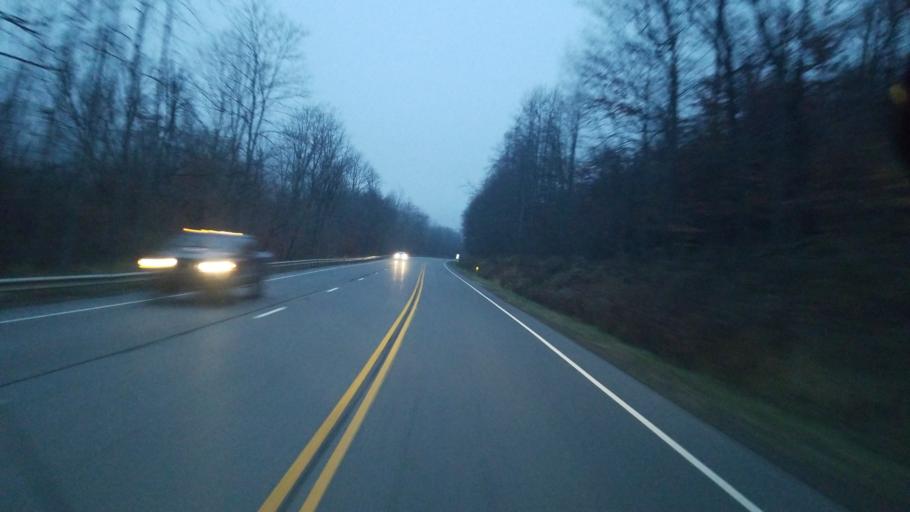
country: US
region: Pennsylvania
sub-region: McKean County
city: Smethport
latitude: 41.7147
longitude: -78.6029
